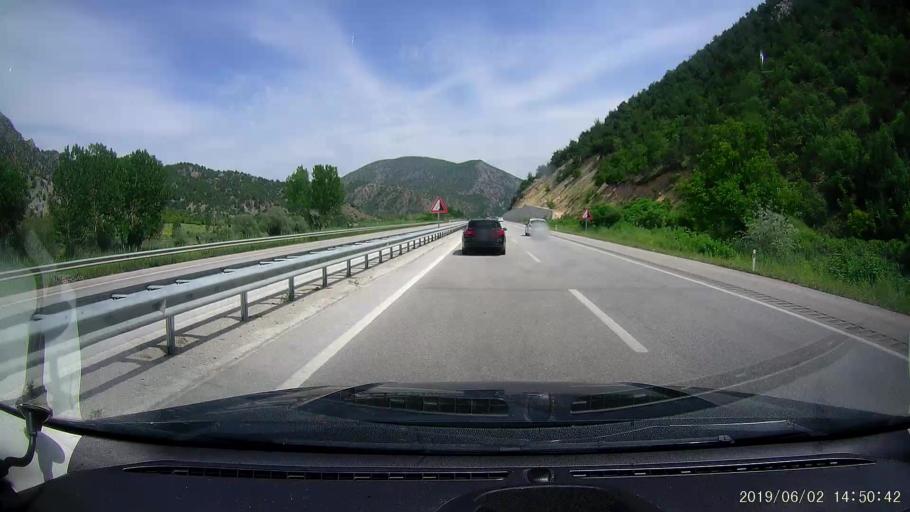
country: TR
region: Corum
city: Kargi
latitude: 41.0699
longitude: 34.5257
